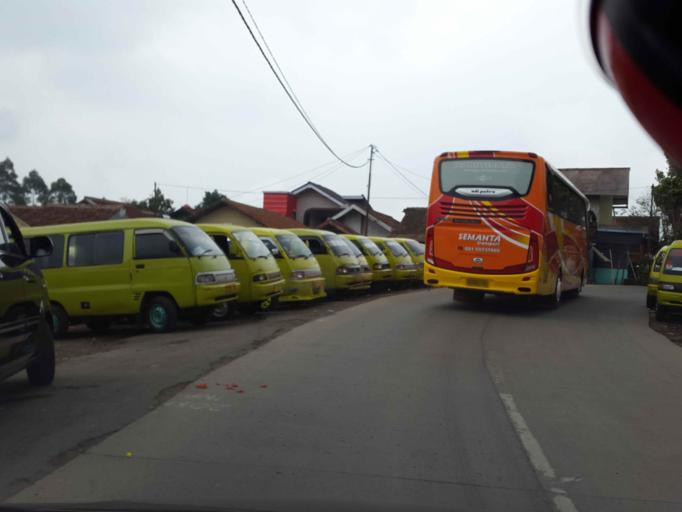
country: ID
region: West Java
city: Lembang
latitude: -6.7986
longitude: 107.5761
